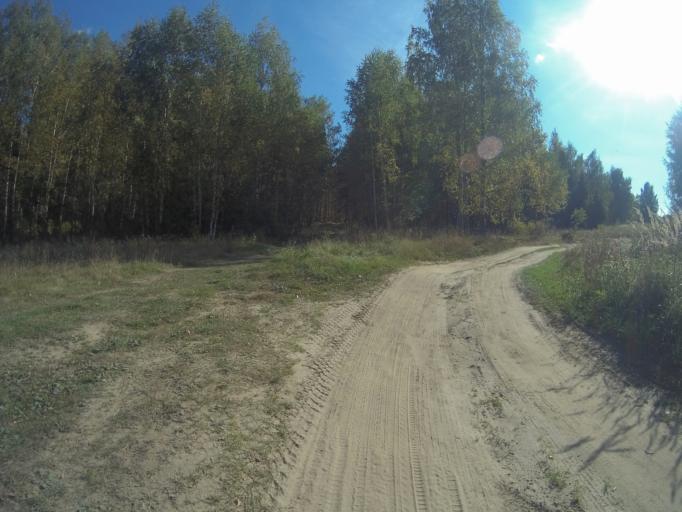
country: RU
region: Vladimir
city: Golovino
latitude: 56.0038
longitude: 40.4419
